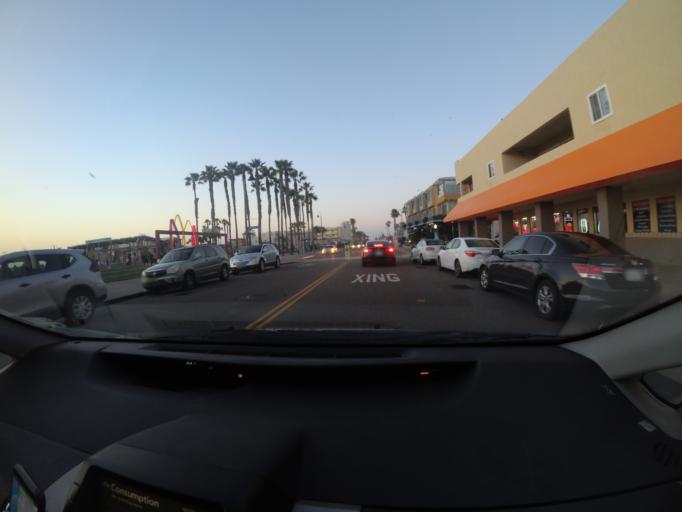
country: US
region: California
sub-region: San Diego County
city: Imperial Beach
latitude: 32.5792
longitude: -117.1316
